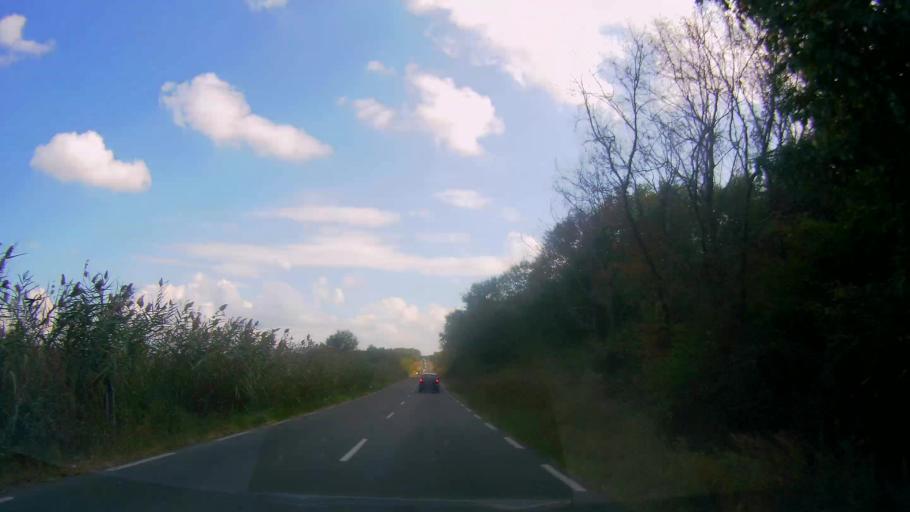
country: BG
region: Burgas
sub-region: Obshtina Kameno
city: Kameno
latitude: 42.4868
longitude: 27.3410
